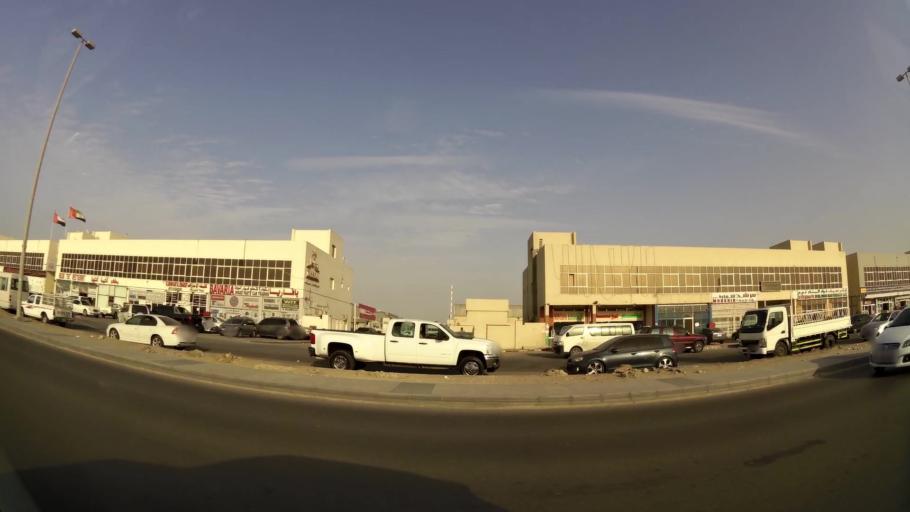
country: AE
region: Abu Dhabi
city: Abu Dhabi
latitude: 24.3658
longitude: 54.5166
